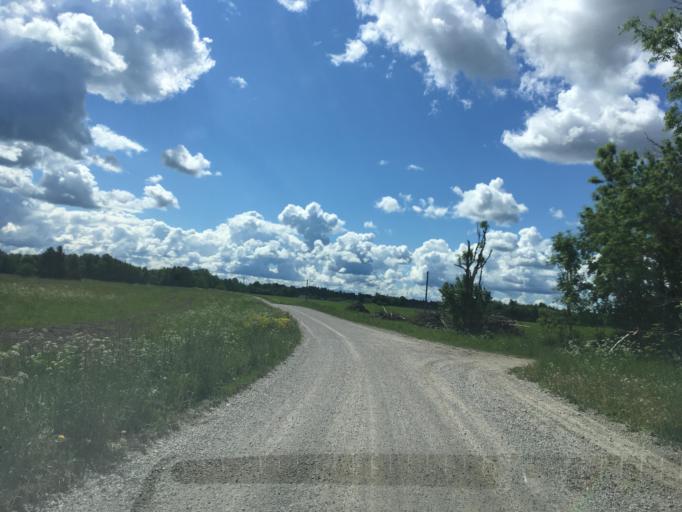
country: EE
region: Harju
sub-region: Nissi vald
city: Turba
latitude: 59.0239
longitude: 24.1994
